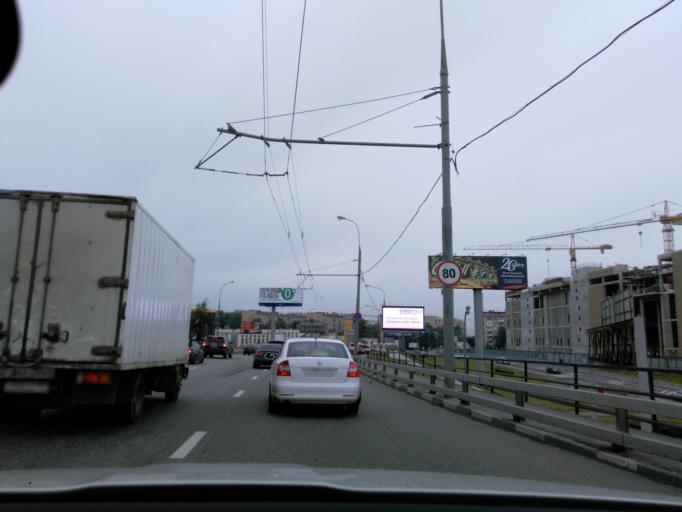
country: RU
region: Moscow
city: Nagornyy
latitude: 55.6631
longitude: 37.6318
